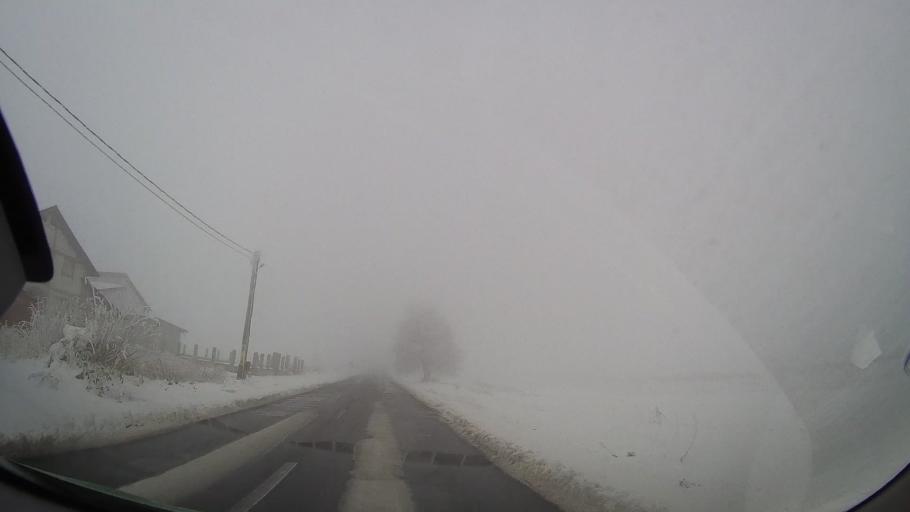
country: RO
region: Neamt
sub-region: Comuna Sabaoani
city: Sabaoani
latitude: 47.0305
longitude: 26.8579
